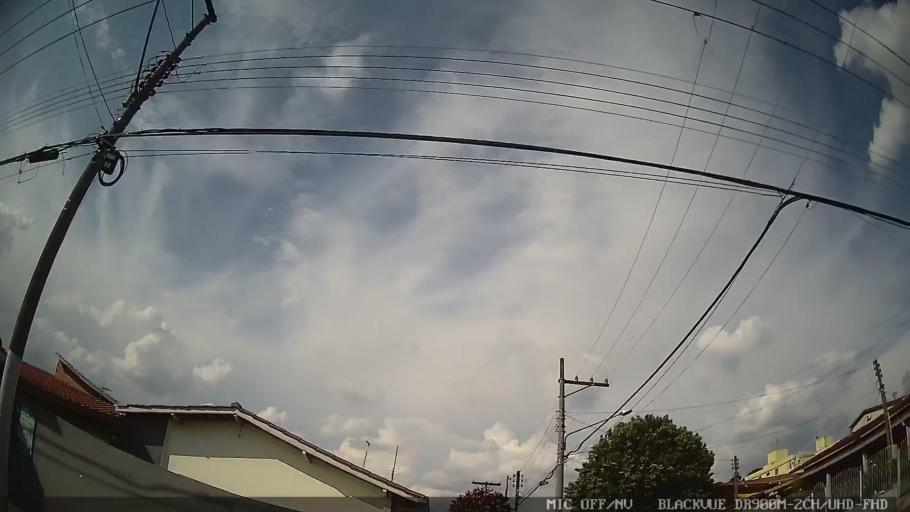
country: BR
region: Sao Paulo
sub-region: Braganca Paulista
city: Braganca Paulista
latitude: -22.9429
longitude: -46.5328
